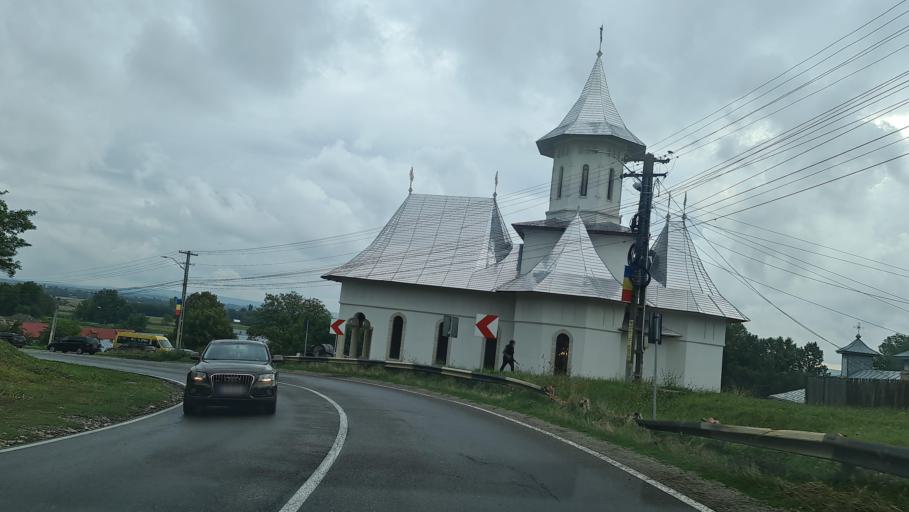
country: RO
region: Neamt
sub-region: Comuna Borlesti
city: Ruseni
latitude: 46.7947
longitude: 26.5377
